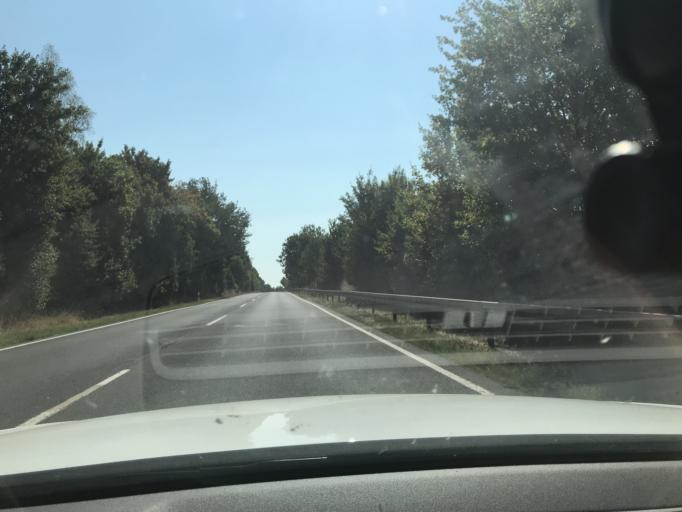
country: DE
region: Bavaria
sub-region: Upper Palatinate
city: Auerbach
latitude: 49.6870
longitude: 11.6282
